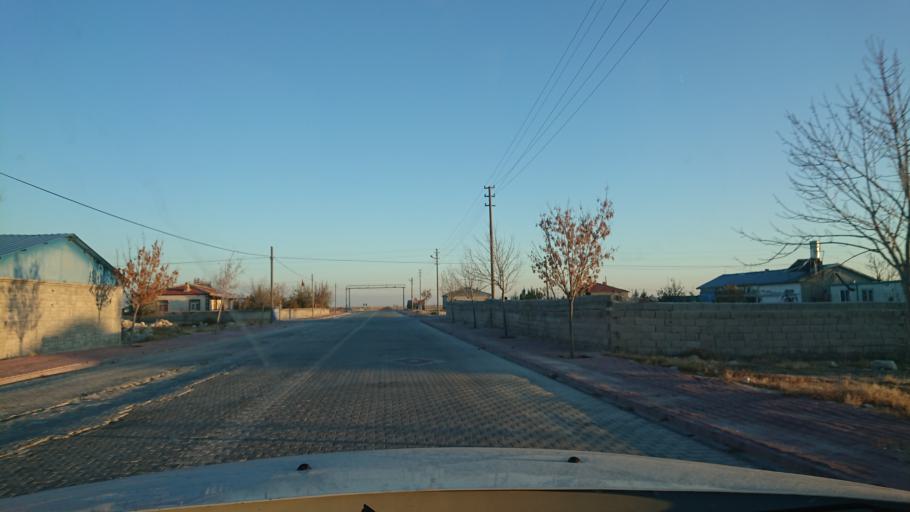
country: TR
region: Aksaray
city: Eskil
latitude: 38.3944
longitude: 33.4251
